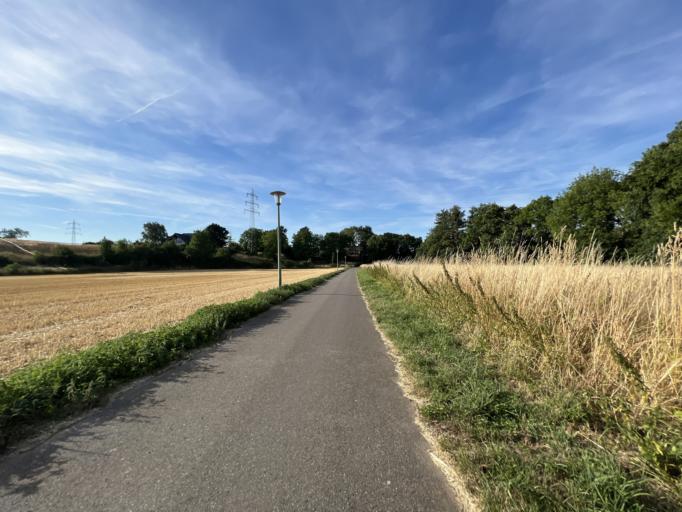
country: DE
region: North Rhine-Westphalia
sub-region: Regierungsbezirk Koln
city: Kreuzau
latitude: 50.7585
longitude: 6.4791
